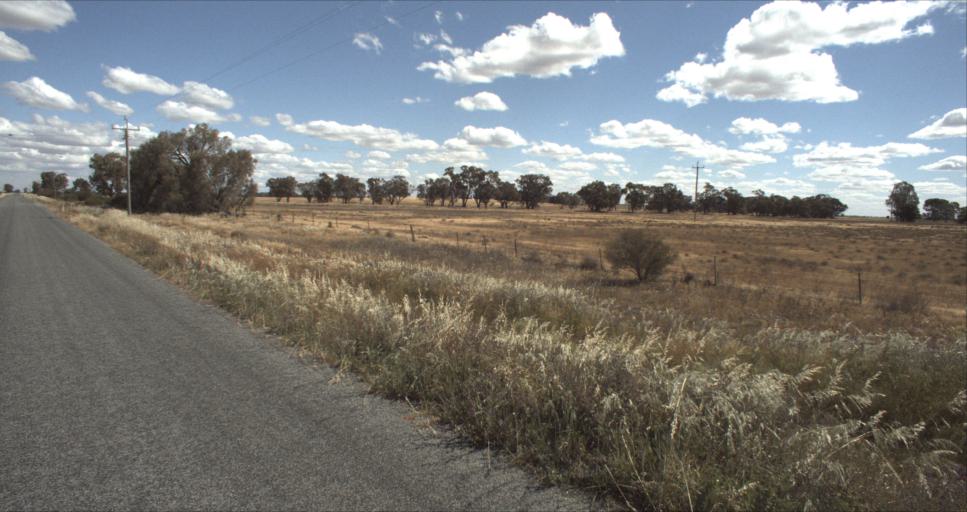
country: AU
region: New South Wales
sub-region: Leeton
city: Leeton
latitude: -34.4867
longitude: 146.2481
